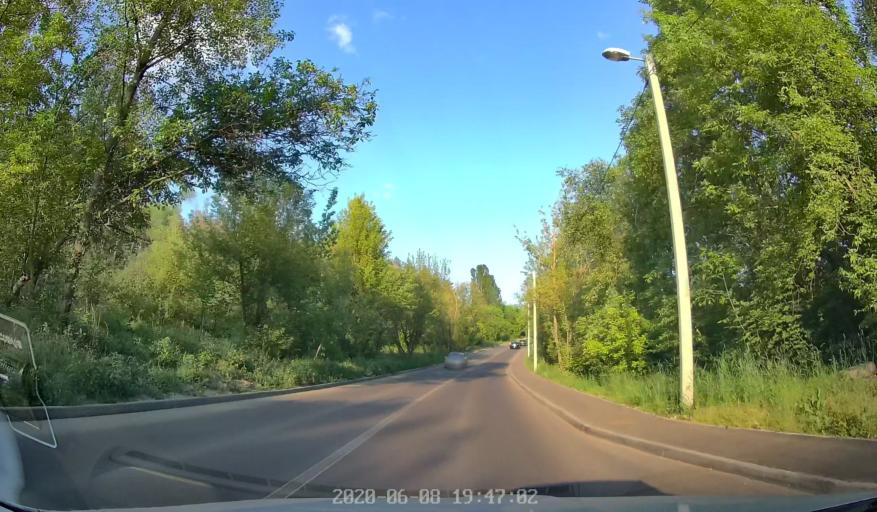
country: MD
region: Chisinau
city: Stauceni
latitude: 47.0610
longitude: 28.8833
